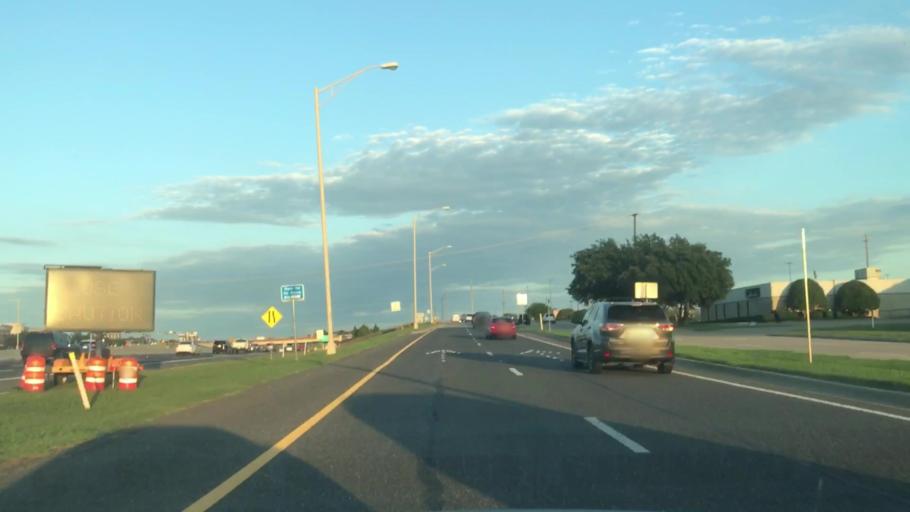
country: US
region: Texas
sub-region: Dallas County
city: Carrollton
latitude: 32.9829
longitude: -96.9147
